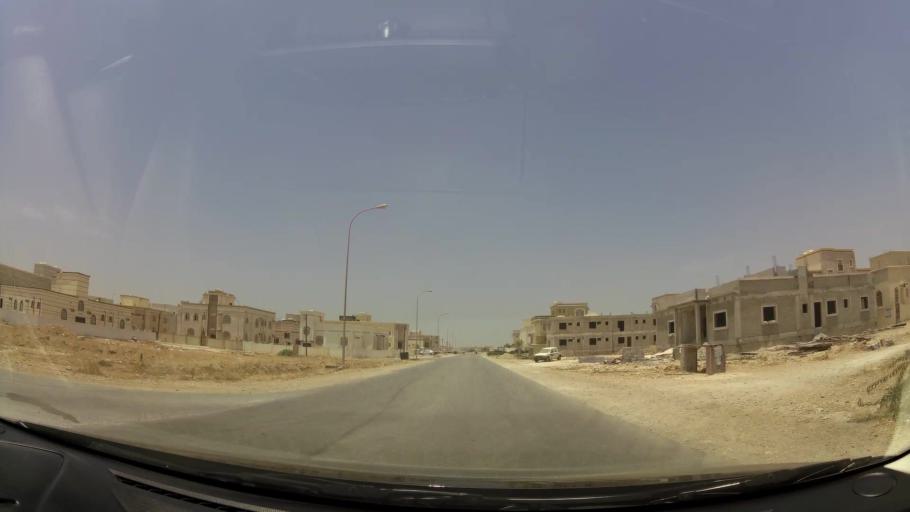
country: OM
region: Zufar
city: Salalah
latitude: 17.0896
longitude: 54.1571
